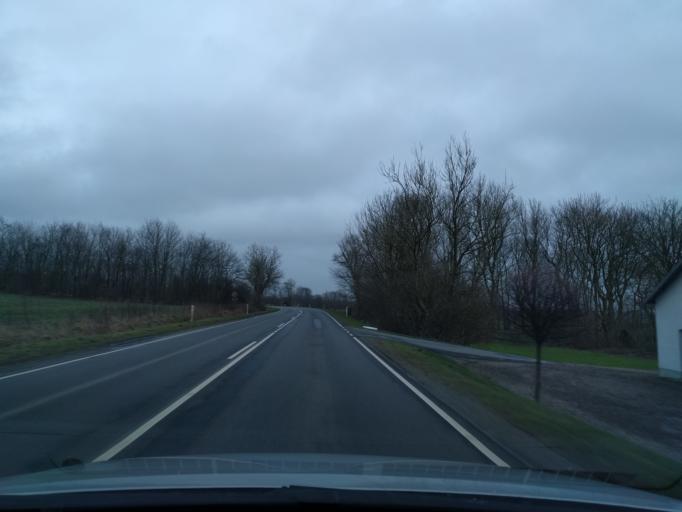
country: DK
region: South Denmark
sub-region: Haderslev Kommune
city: Vojens
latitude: 55.2422
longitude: 9.2149
